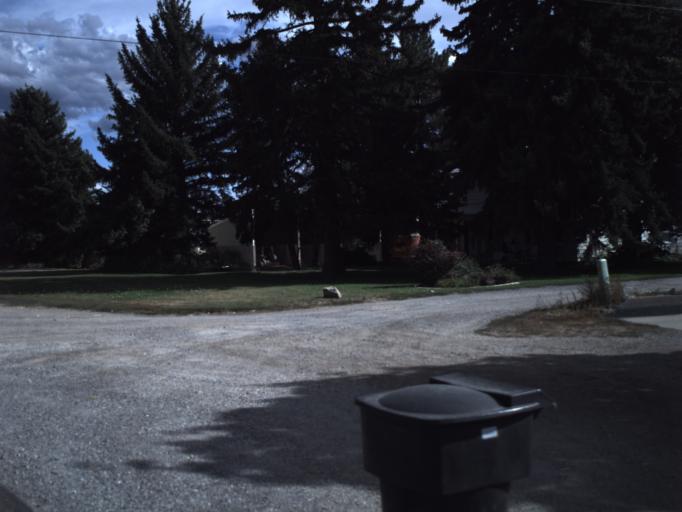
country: US
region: Utah
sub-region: Cache County
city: Wellsville
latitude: 41.6437
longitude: -111.9087
